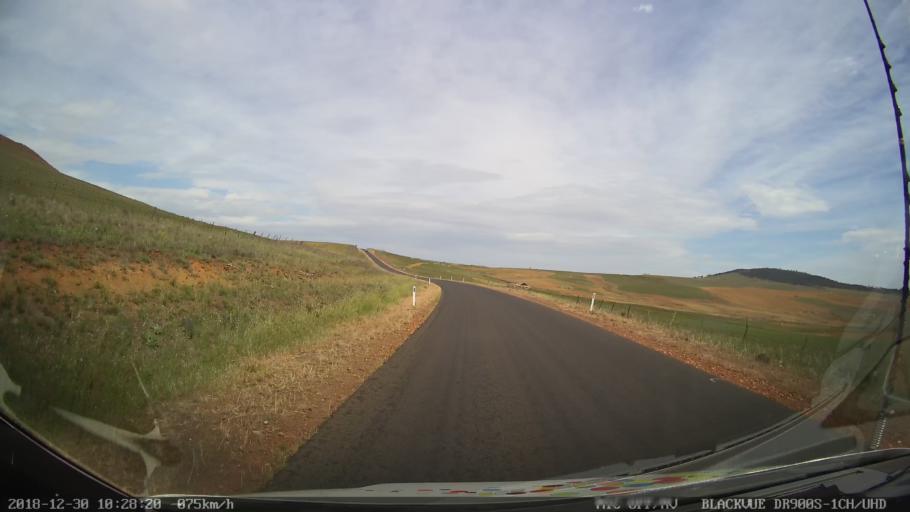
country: AU
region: New South Wales
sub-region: Snowy River
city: Berridale
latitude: -36.5061
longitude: 148.9234
